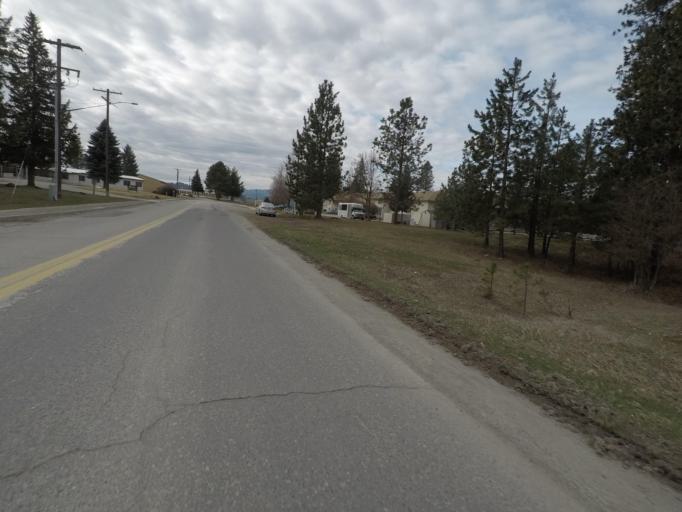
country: US
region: Washington
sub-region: Stevens County
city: Colville
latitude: 48.5441
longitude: -117.8881
